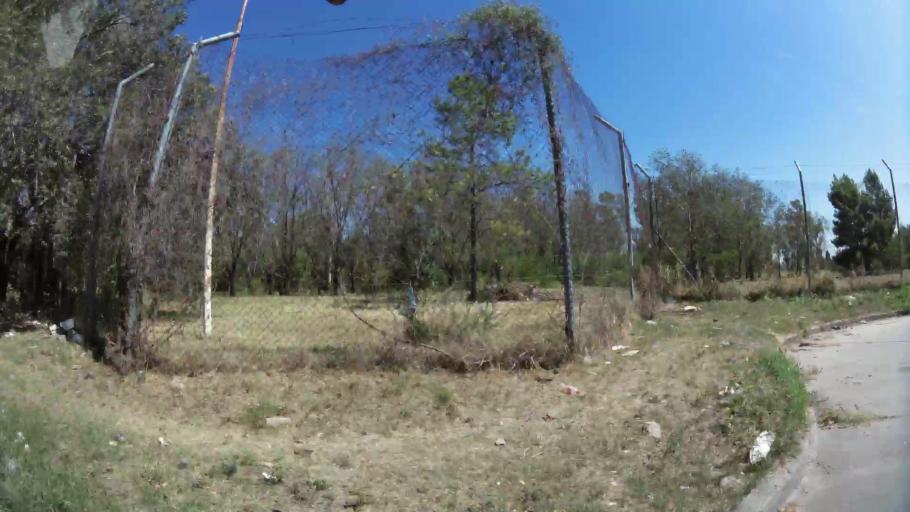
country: AR
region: Cordoba
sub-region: Departamento de Capital
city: Cordoba
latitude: -31.4548
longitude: -64.1628
